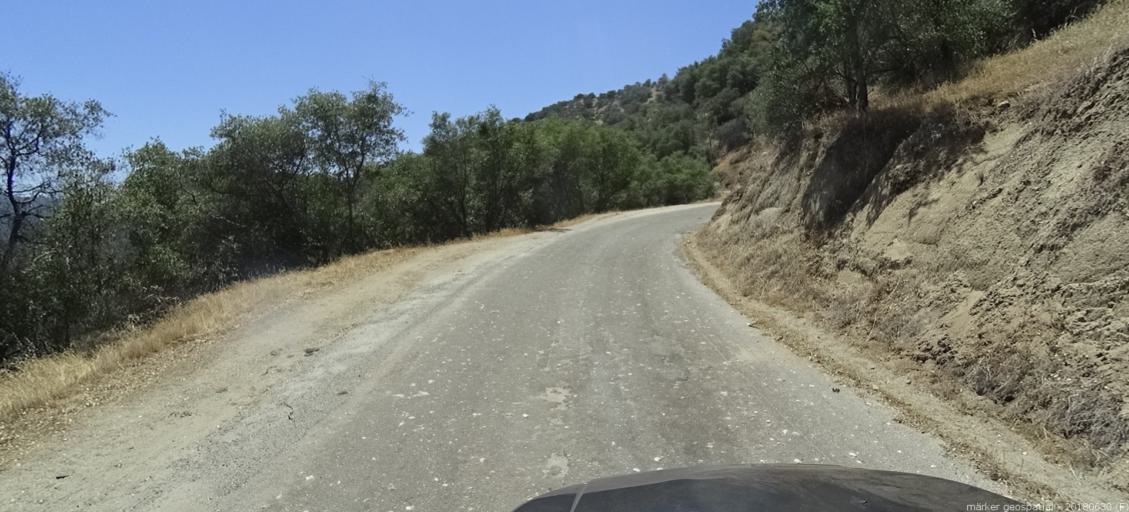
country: US
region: California
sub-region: Fresno County
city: Auberry
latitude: 37.1674
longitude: -119.4388
